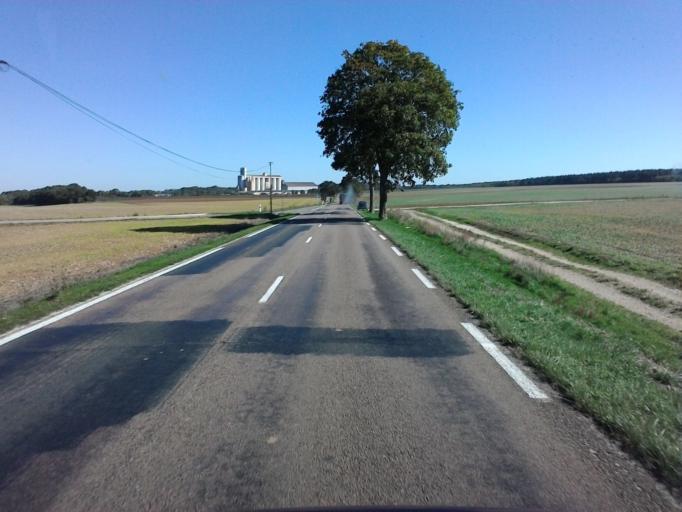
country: FR
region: Champagne-Ardenne
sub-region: Departement de la Haute-Marne
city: Chaumont
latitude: 48.1066
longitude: 5.0750
